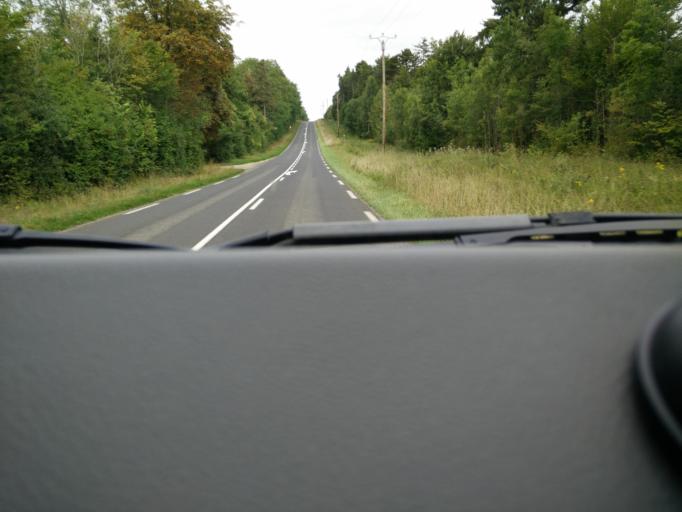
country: FR
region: Lorraine
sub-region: Departement de Meurthe-et-Moselle
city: Montauville
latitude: 48.9145
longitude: 5.9222
